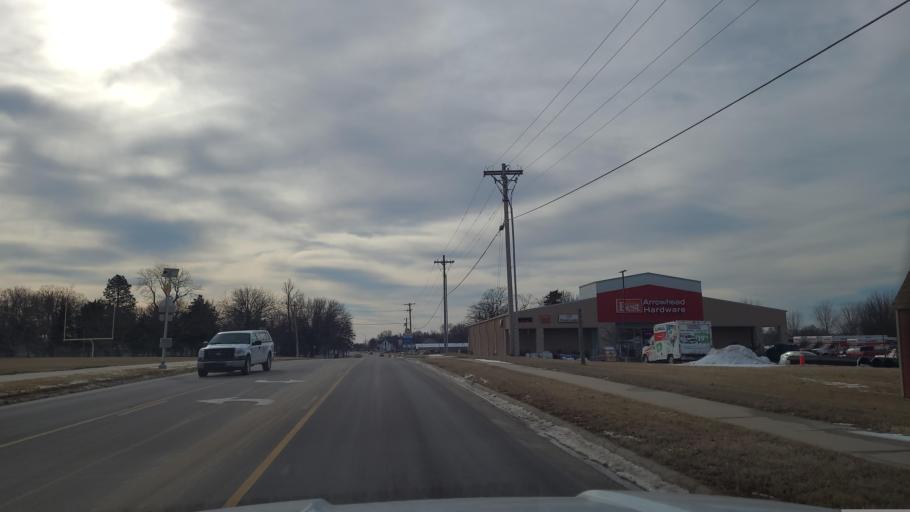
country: US
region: Kansas
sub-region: Douglas County
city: Baldwin City
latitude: 38.7862
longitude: -95.1865
